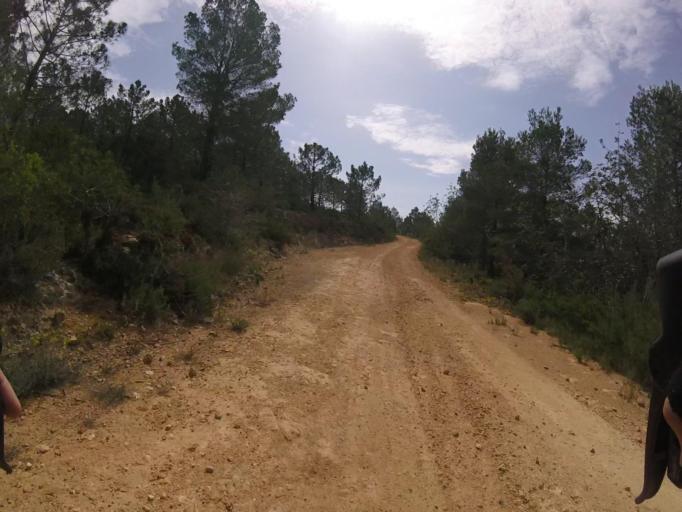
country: ES
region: Valencia
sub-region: Provincia de Castello
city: Cuevas de Vinroma
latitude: 40.2848
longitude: 0.1189
